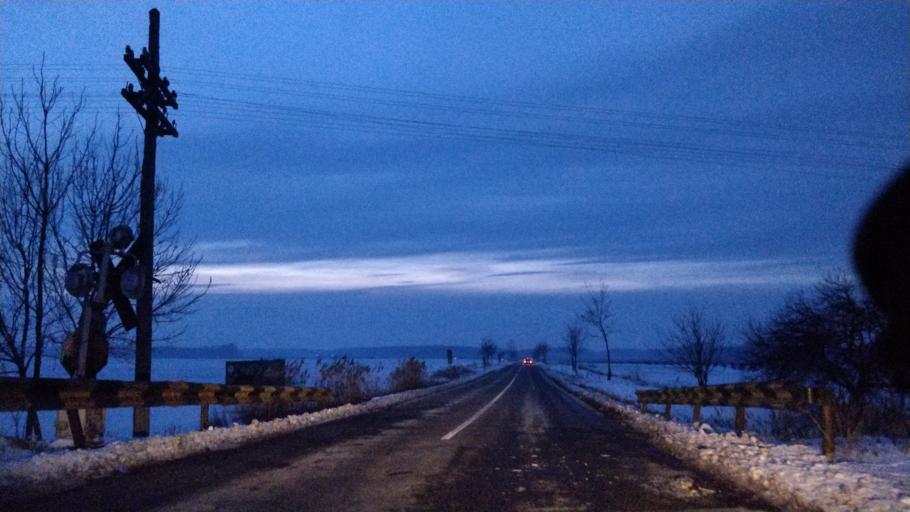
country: RO
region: Vrancea
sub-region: Comuna Suraia
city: Suraia
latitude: 45.6462
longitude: 27.3547
